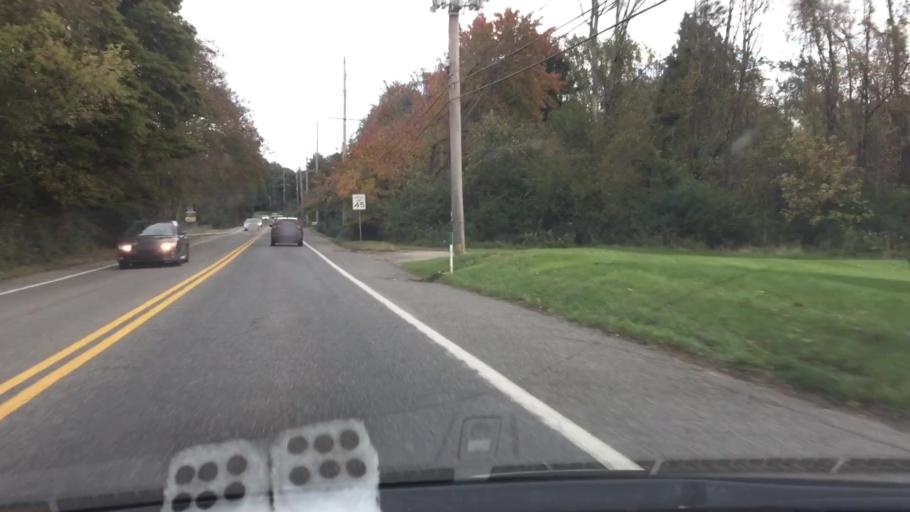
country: US
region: Pennsylvania
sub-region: Delaware County
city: Chester Heights
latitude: 39.9445
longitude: -75.4988
